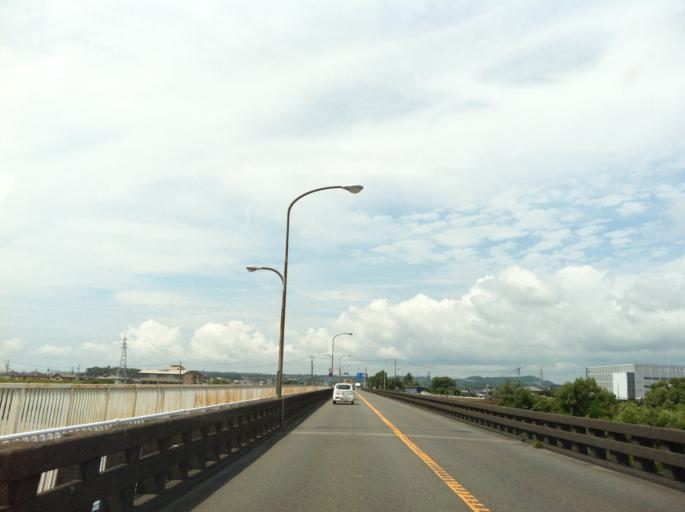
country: JP
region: Shizuoka
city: Fujieda
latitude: 34.7957
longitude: 138.2558
